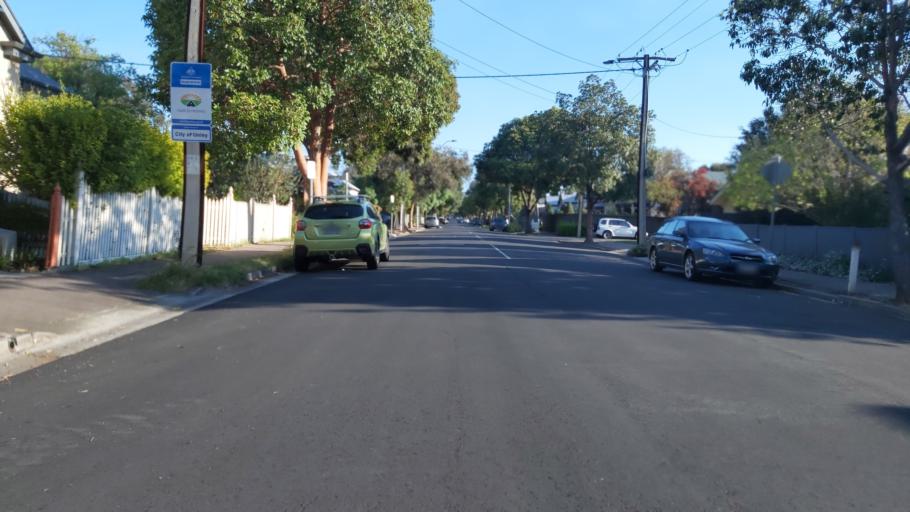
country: AU
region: South Australia
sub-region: Unley
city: Fullarton
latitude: -34.9471
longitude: 138.6213
